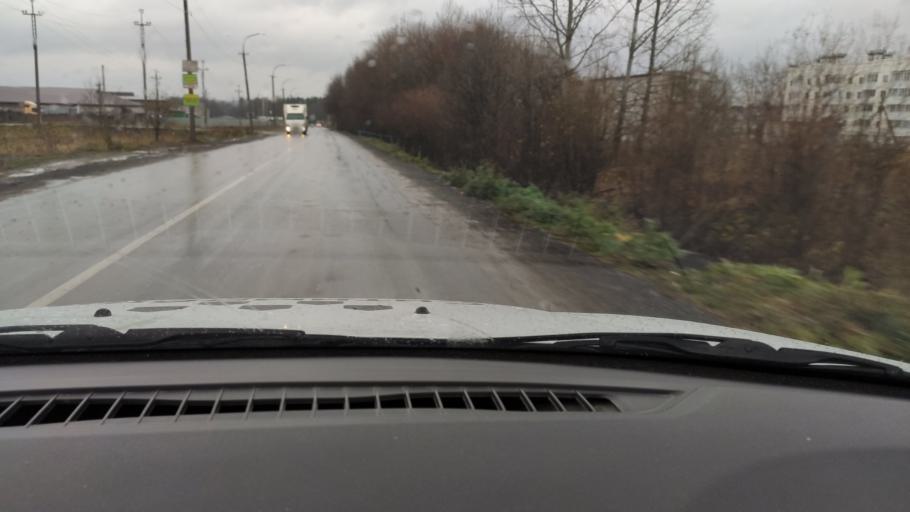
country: RU
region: Perm
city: Sylva
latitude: 58.0270
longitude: 56.7390
